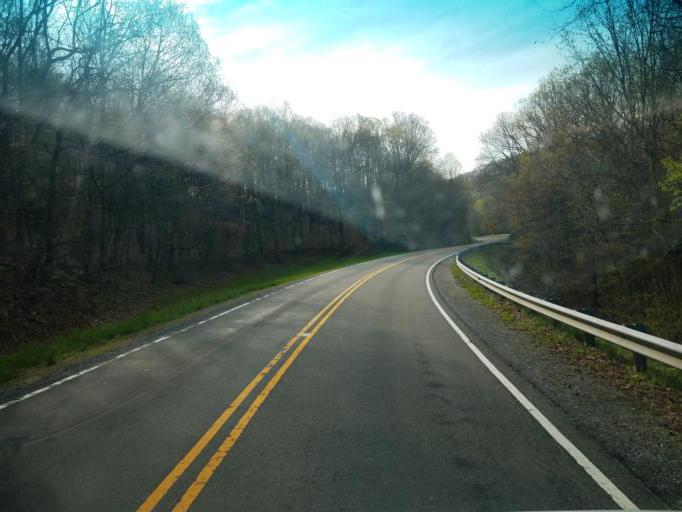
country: US
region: Virginia
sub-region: Smyth County
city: Atkins
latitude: 36.8114
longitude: -81.4195
